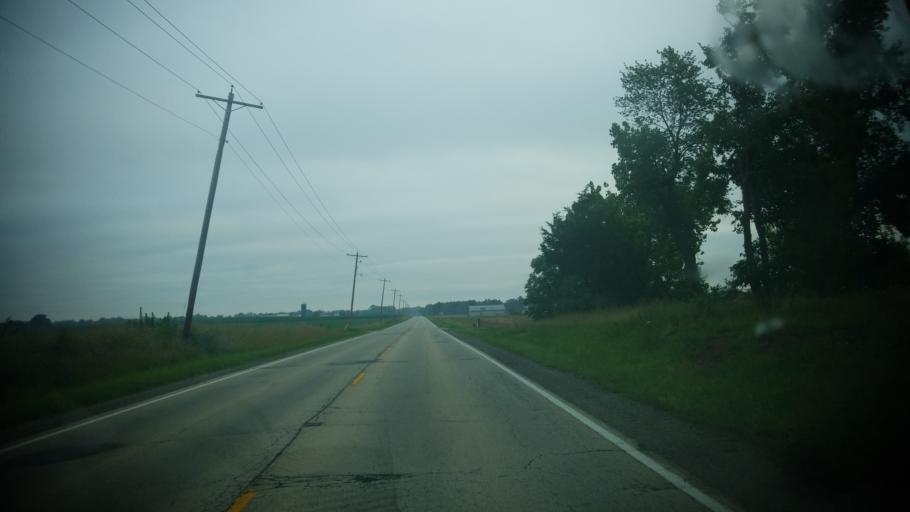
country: US
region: Illinois
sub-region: Clay County
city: Flora
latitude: 38.6580
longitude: -88.4383
